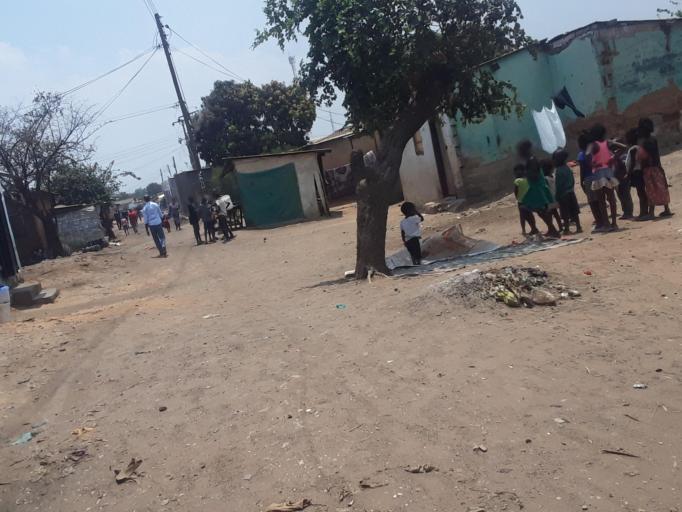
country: ZM
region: Lusaka
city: Lusaka
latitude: -15.3645
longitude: 28.2996
